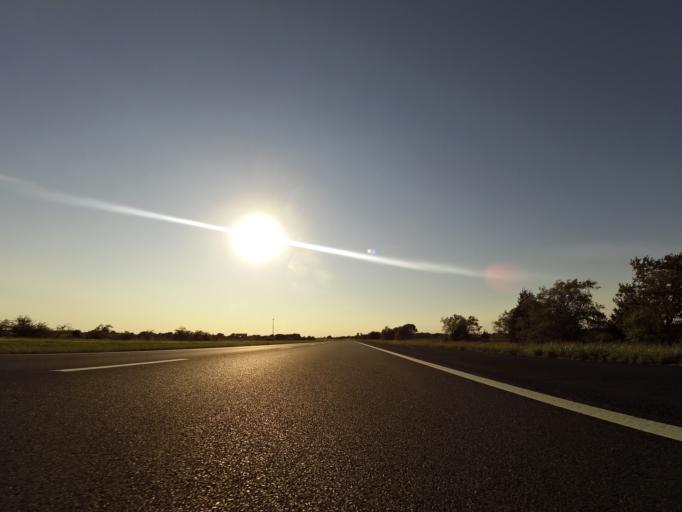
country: US
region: Kansas
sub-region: Reno County
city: Haven
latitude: 37.8918
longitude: -97.7566
